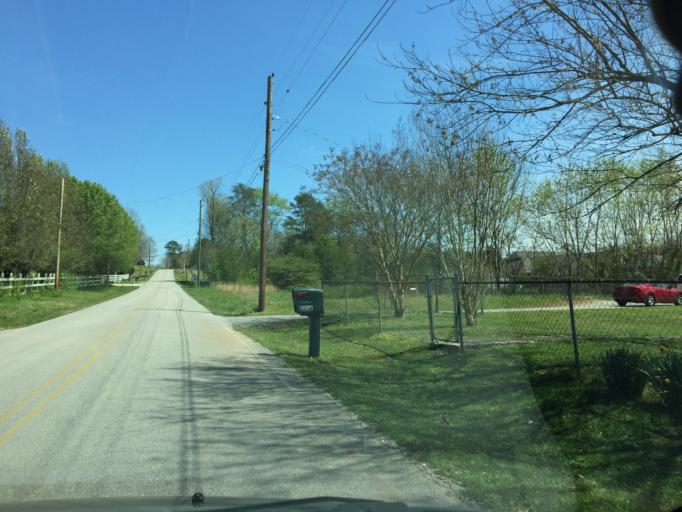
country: US
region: Tennessee
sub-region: Hamilton County
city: Soddy-Daisy
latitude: 35.2331
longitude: -85.2086
